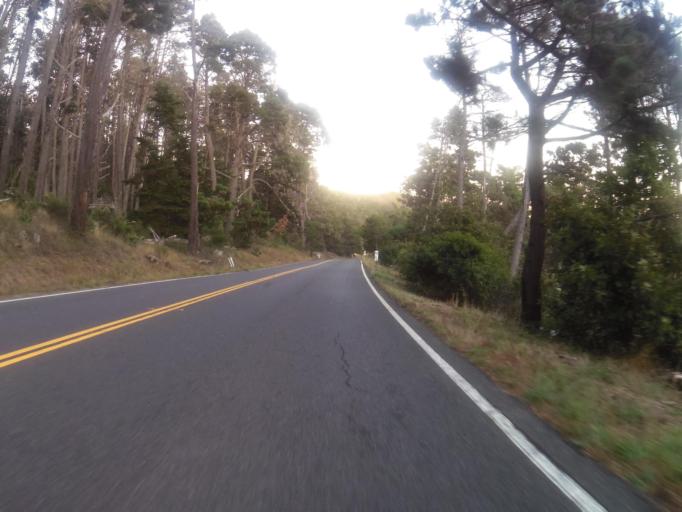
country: US
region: California
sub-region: Sonoma County
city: Sea Ranch
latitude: 38.6029
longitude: -123.3552
